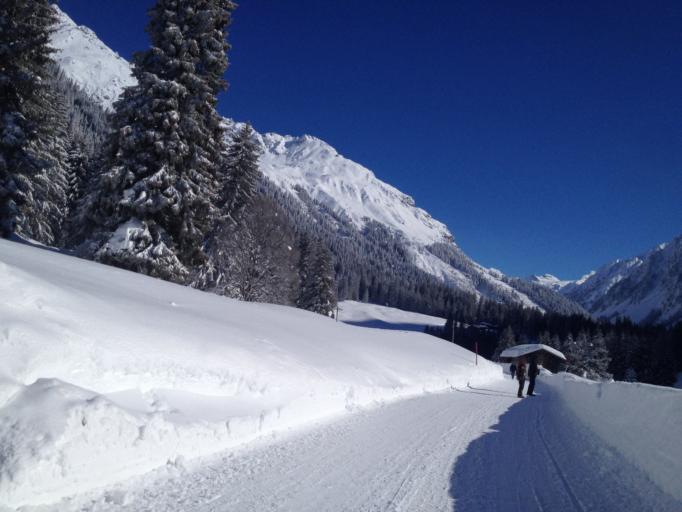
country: CH
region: Grisons
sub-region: Praettigau/Davos District
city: Klosters Serneus
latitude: 46.8601
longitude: 9.9271
